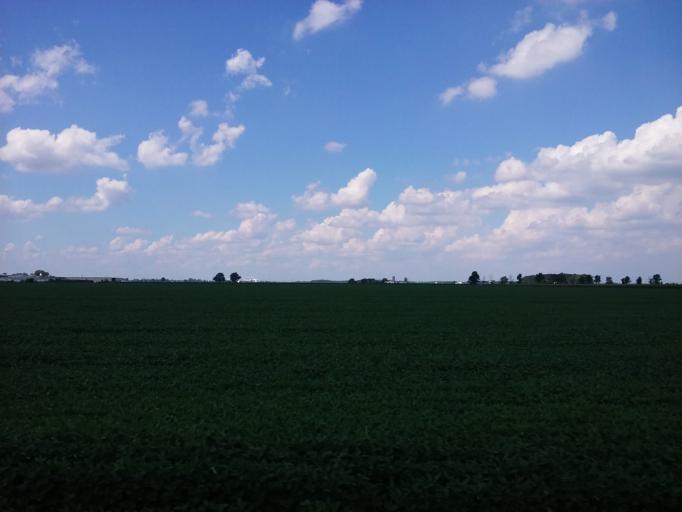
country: US
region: Ohio
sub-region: Wood County
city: Bowling Green
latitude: 41.3743
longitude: -83.5972
